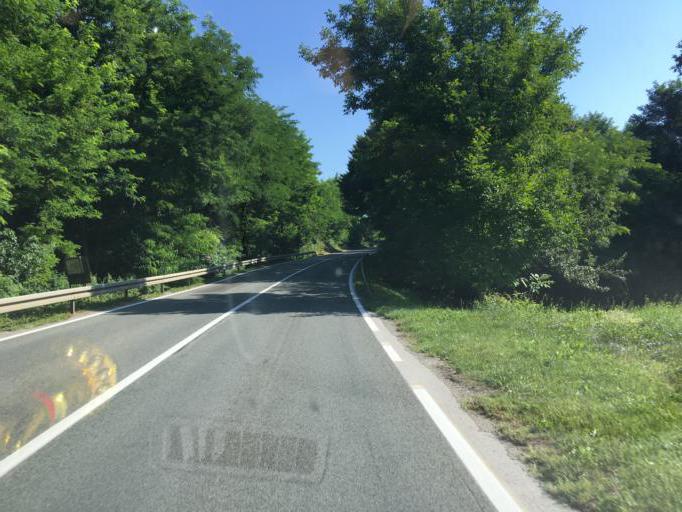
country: HR
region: Karlovacka
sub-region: Grad Karlovac
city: Slunj
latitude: 45.1566
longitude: 15.5591
